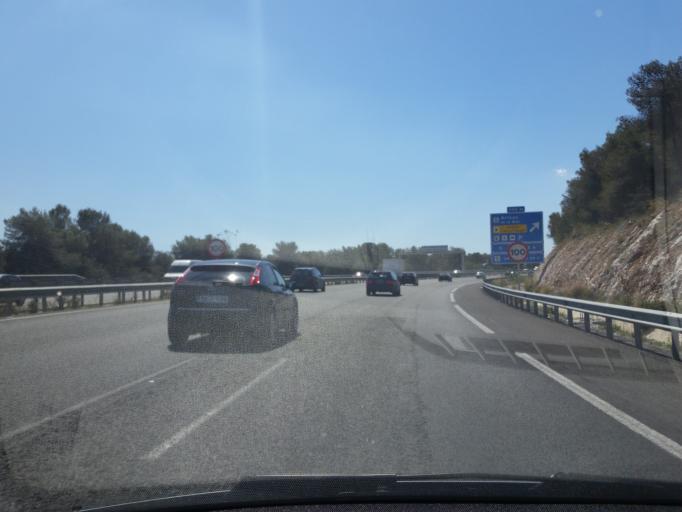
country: ES
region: Andalusia
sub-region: Provincia de Malaga
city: Torremolinos
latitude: 36.6170
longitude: -4.5194
